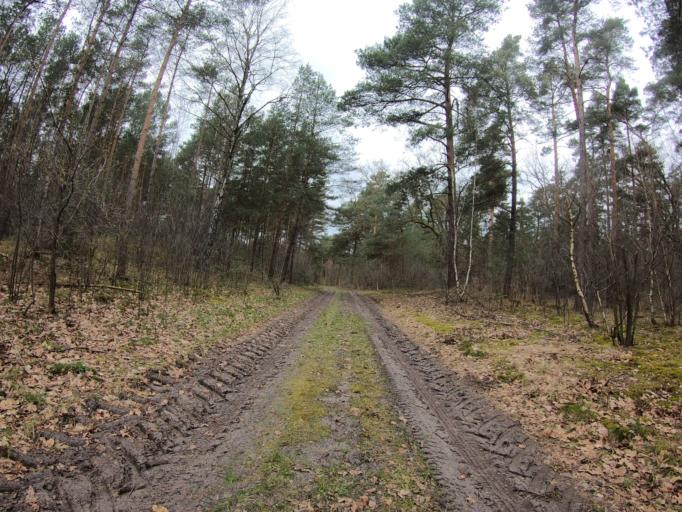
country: DE
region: Lower Saxony
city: Leiferde
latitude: 52.4853
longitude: 10.4506
